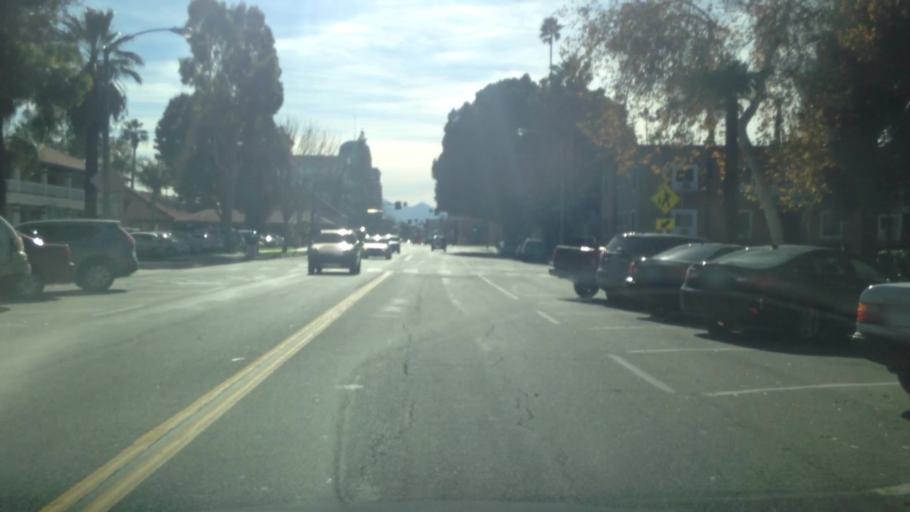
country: US
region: California
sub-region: Riverside County
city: Rubidoux
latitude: 33.9827
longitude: -117.3694
